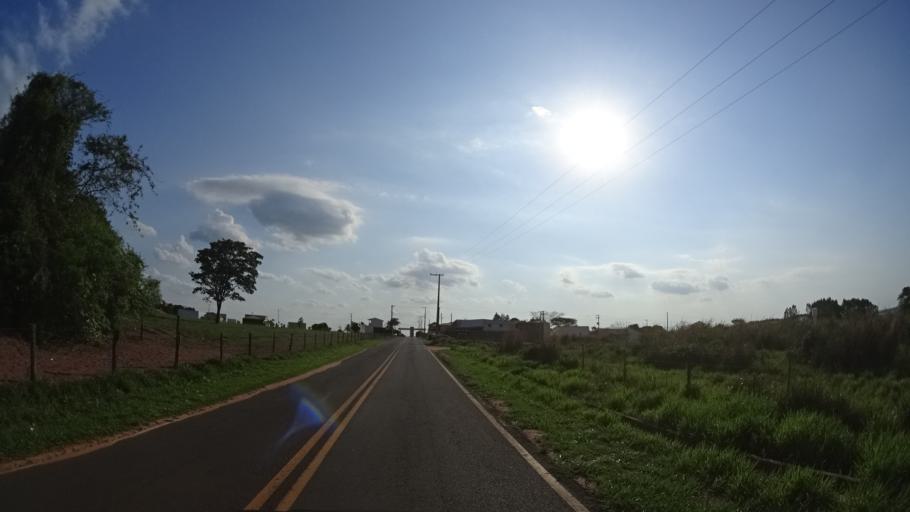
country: BR
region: Sao Paulo
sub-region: Novo Horizonte
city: Novo Horizonte
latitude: -21.4074
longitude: -49.5274
